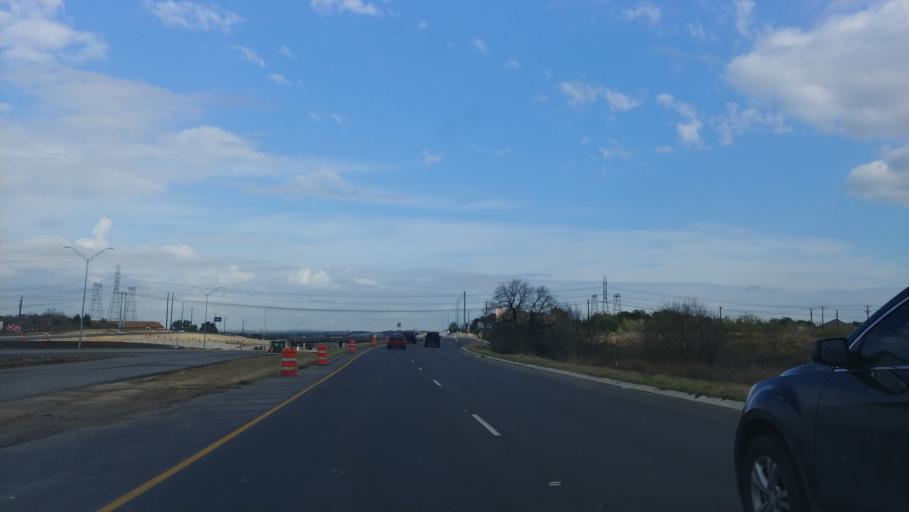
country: US
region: Texas
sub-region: Bexar County
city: Lackland Air Force Base
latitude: 29.4116
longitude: -98.7093
